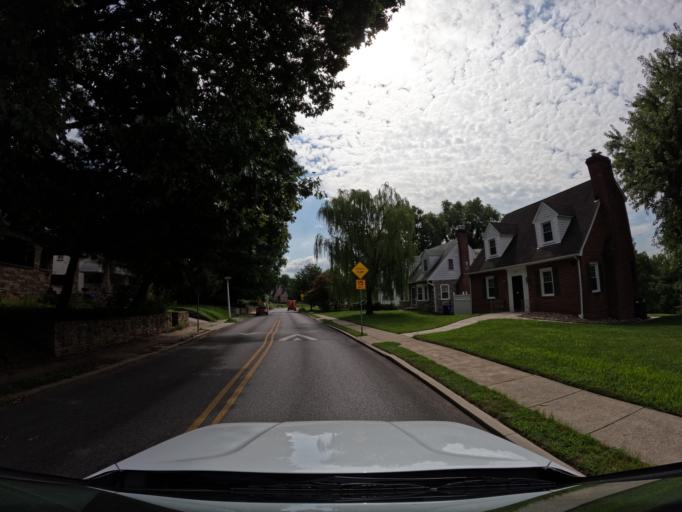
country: US
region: Maryland
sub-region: Baltimore County
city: Parkville
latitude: 39.3337
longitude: -76.5715
